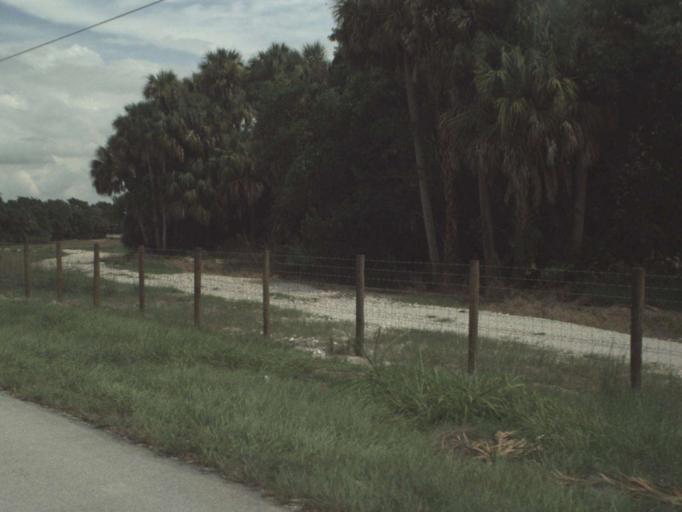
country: US
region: Florida
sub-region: Martin County
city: Indiantown
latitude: 27.0690
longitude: -80.6520
